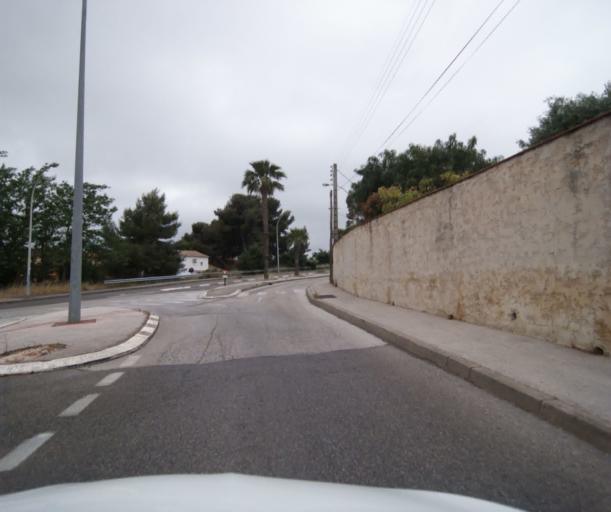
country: FR
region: Provence-Alpes-Cote d'Azur
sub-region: Departement du Var
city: La Seyne-sur-Mer
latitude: 43.0887
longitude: 5.8905
